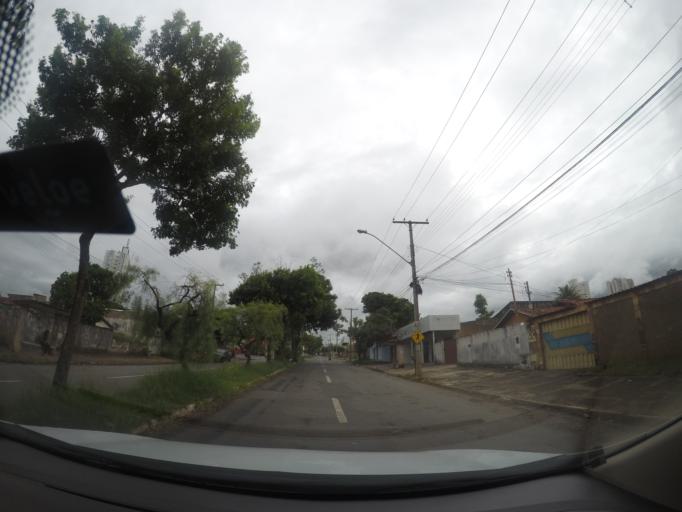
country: BR
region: Goias
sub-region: Goiania
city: Goiania
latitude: -16.7301
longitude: -49.2808
